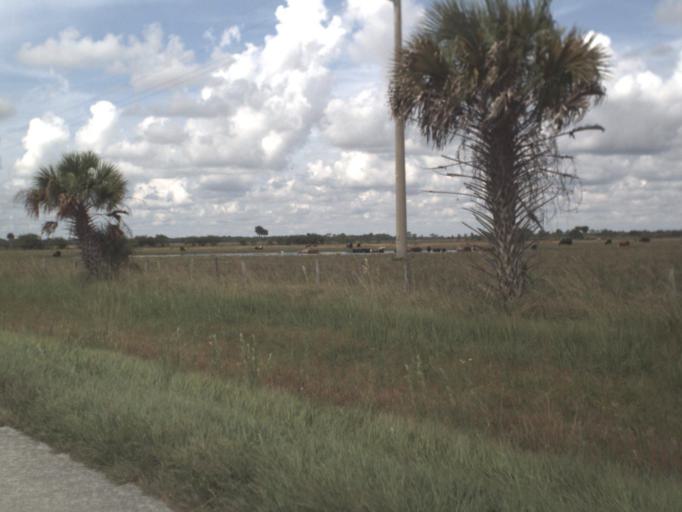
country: US
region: Florida
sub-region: Okeechobee County
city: Okeechobee
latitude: 27.2436
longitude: -80.8759
